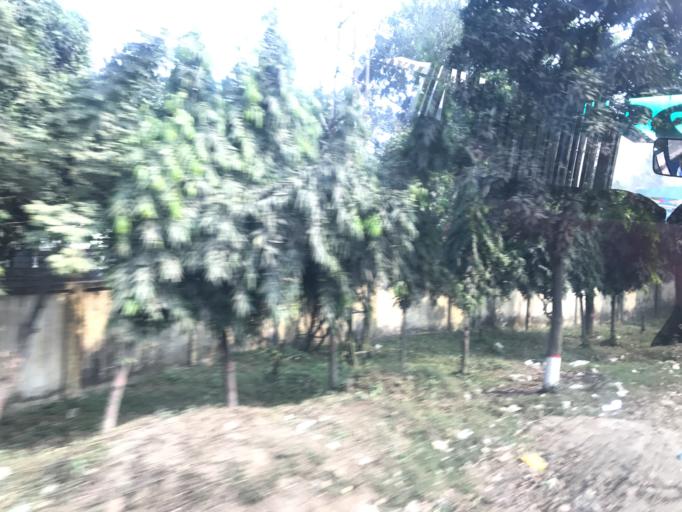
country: BD
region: Dhaka
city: Tungi
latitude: 23.9092
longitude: 90.2640
